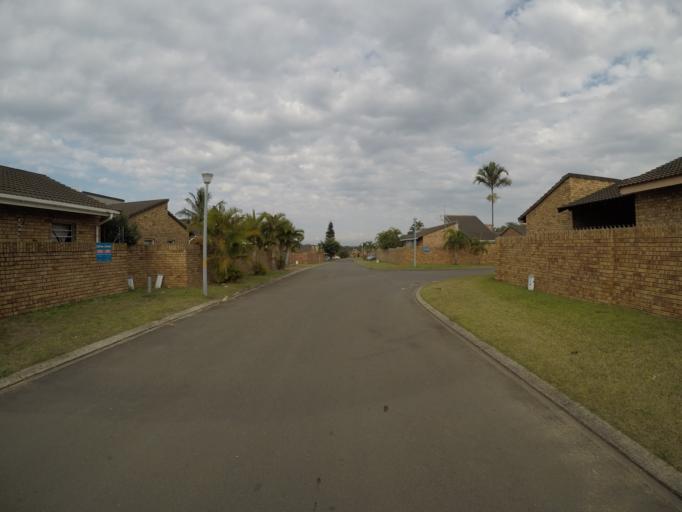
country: ZA
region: KwaZulu-Natal
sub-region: uThungulu District Municipality
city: Richards Bay
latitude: -28.7370
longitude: 32.0839
